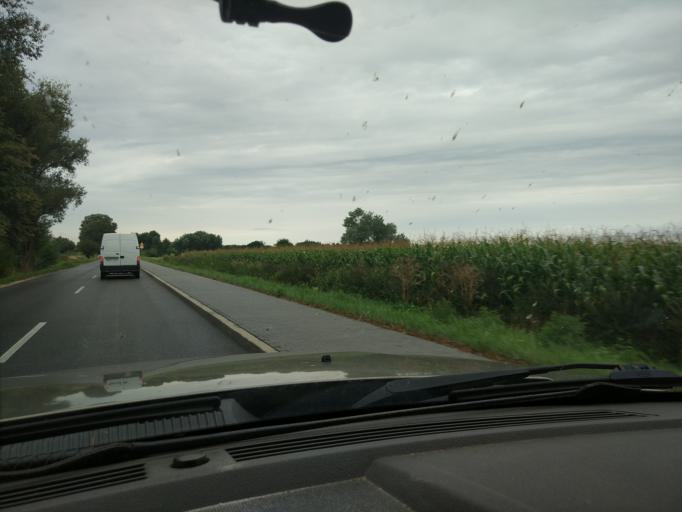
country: PL
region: Masovian Voivodeship
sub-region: Powiat pruszkowski
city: Brwinow
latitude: 52.1592
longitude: 20.7335
